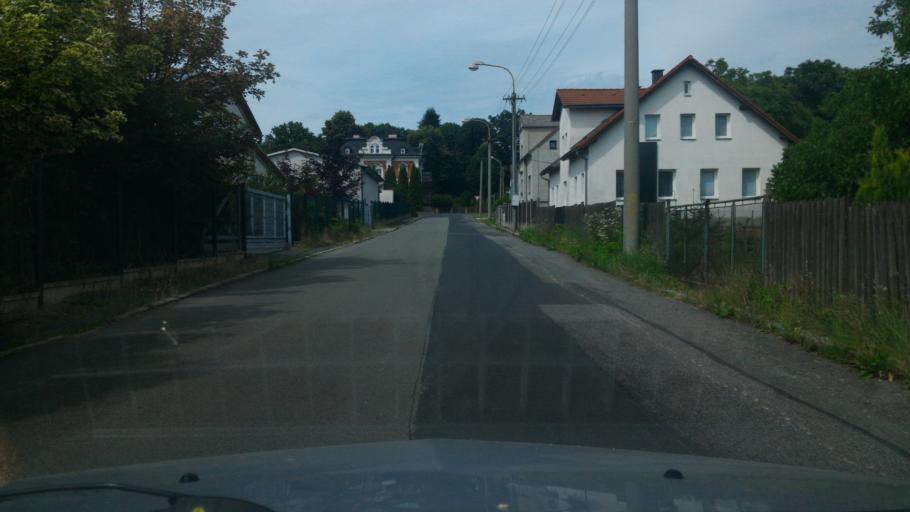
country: CZ
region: Ustecky
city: Varnsdorf
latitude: 50.9091
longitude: 14.6375
